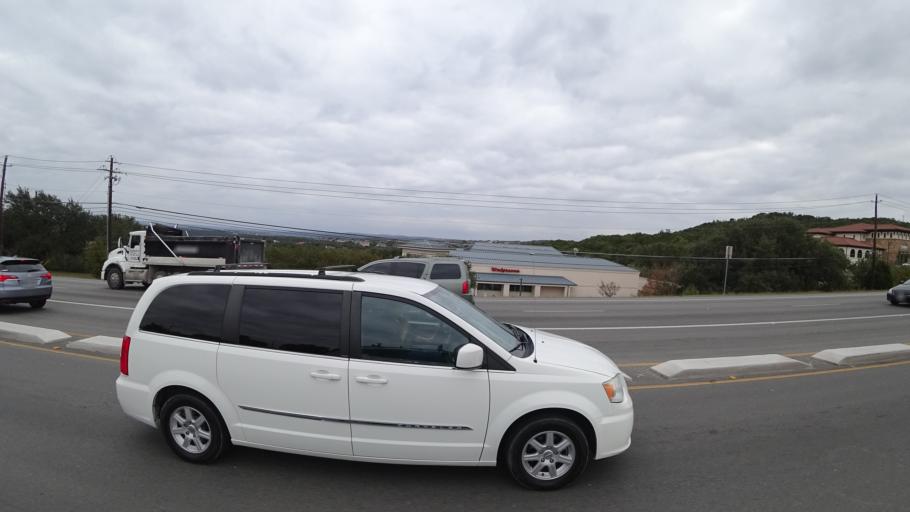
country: US
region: Texas
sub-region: Travis County
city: The Hills
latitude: 30.3403
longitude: -97.9691
